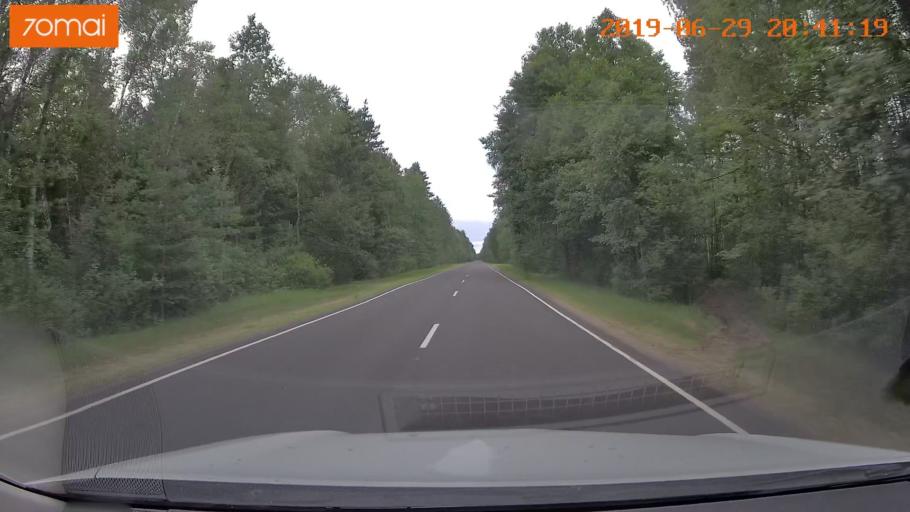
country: BY
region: Brest
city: Hantsavichy
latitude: 52.5842
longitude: 26.3411
